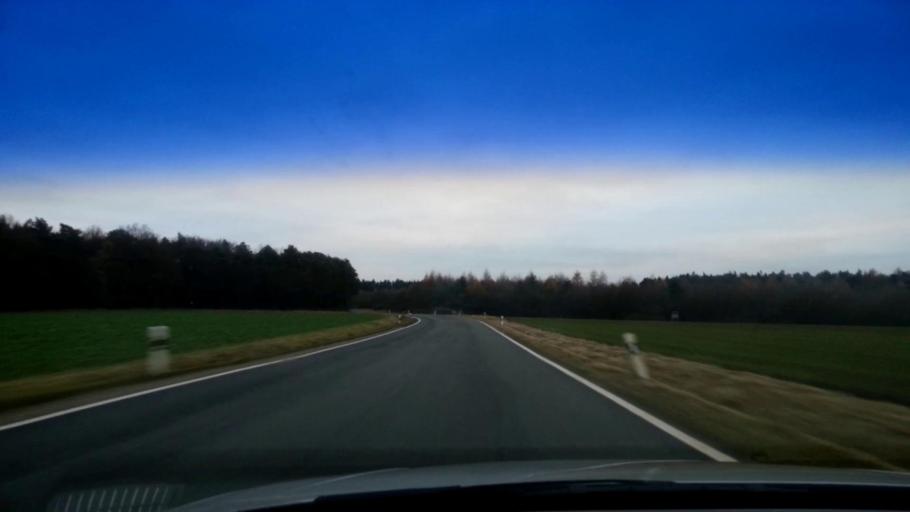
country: DE
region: Bavaria
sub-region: Regierungsbezirk Mittelfranken
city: Muhlhausen
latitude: 49.7976
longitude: 10.7843
